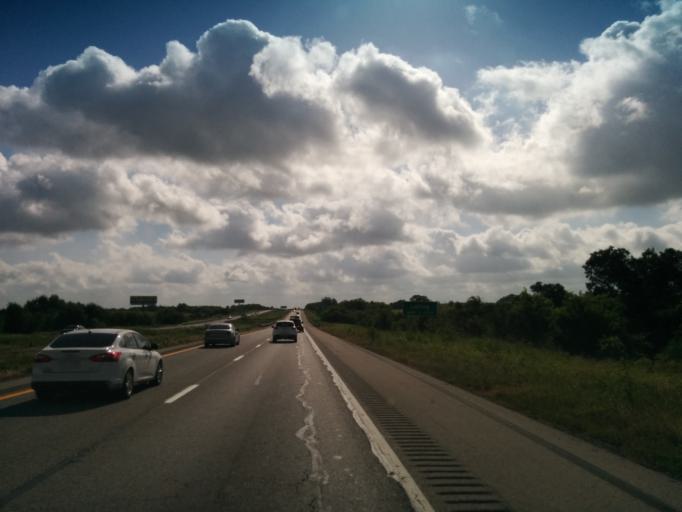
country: US
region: Texas
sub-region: Caldwell County
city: Luling
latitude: 29.6484
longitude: -97.6844
